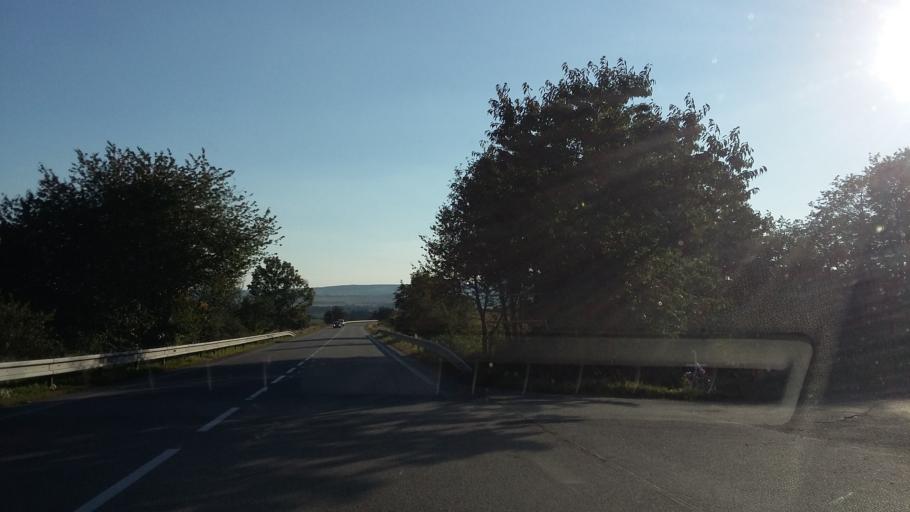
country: CZ
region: Vysocina
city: Luka nad Jihlavou
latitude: 49.3945
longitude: 15.7209
